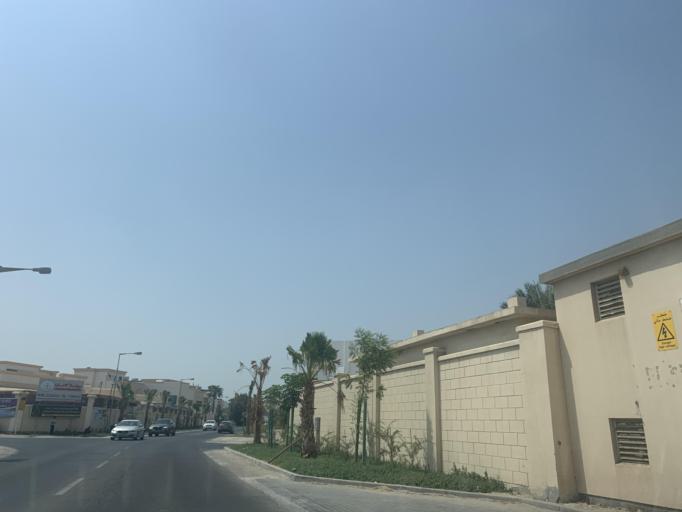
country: BH
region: Manama
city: Jidd Hafs
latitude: 26.2017
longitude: 50.4975
